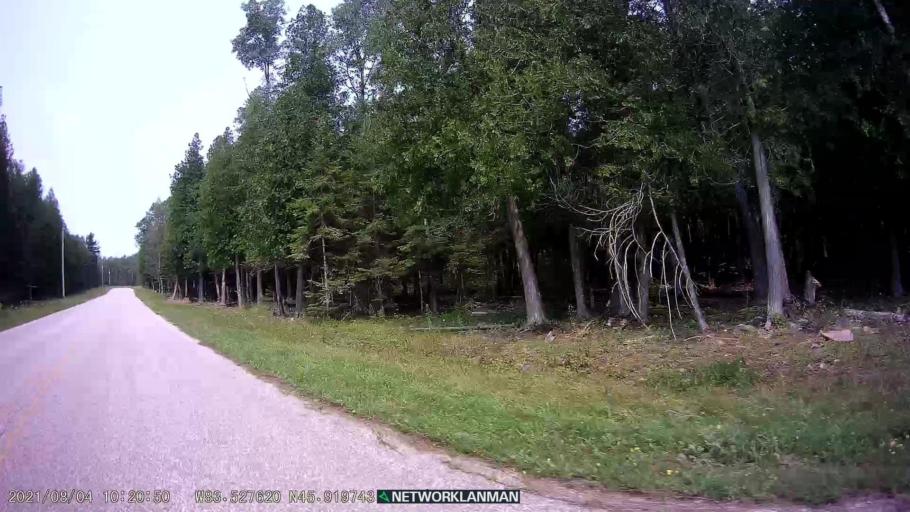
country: CA
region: Ontario
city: Thessalon
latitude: 45.9198
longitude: -83.5277
